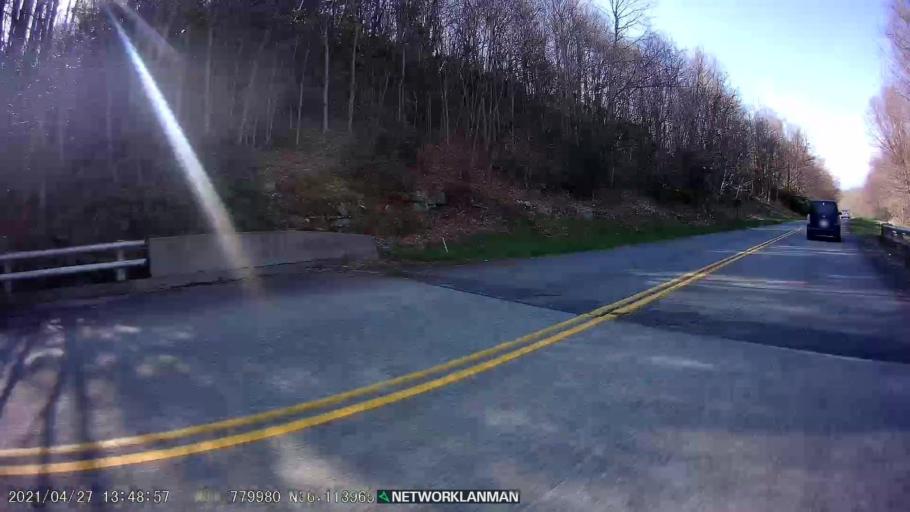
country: US
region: North Carolina
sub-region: Watauga County
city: Foscoe
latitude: 36.1141
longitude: -81.7800
